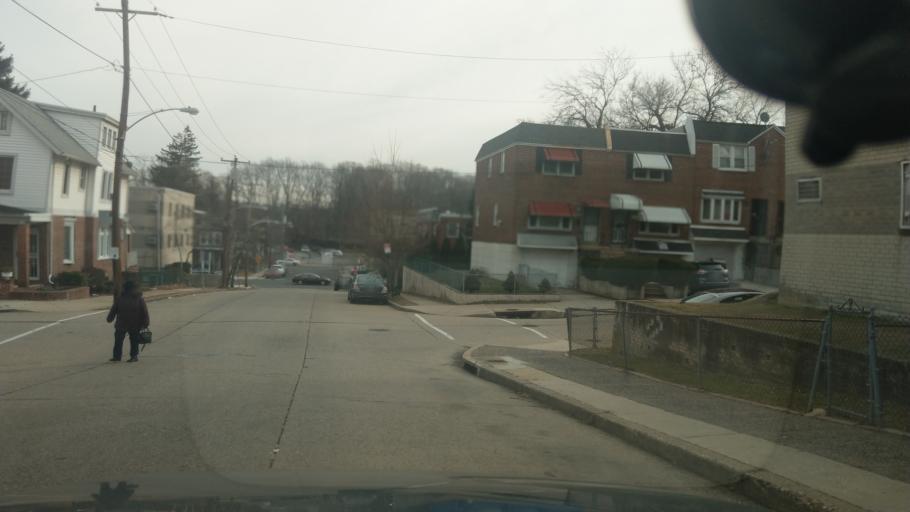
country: US
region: Pennsylvania
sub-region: Montgomery County
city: Wyncote
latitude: 40.0452
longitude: -75.1374
